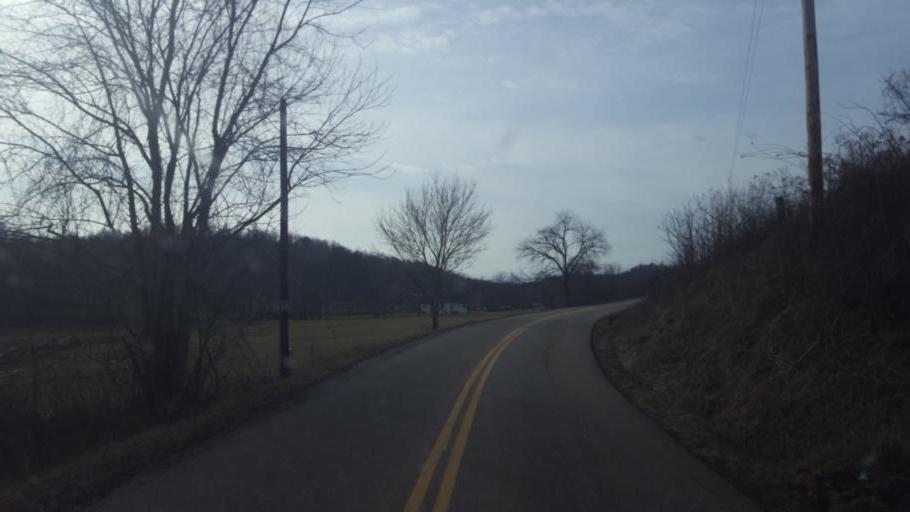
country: US
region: Ohio
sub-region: Gallia County
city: Gallipolis
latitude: 38.7271
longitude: -82.3227
